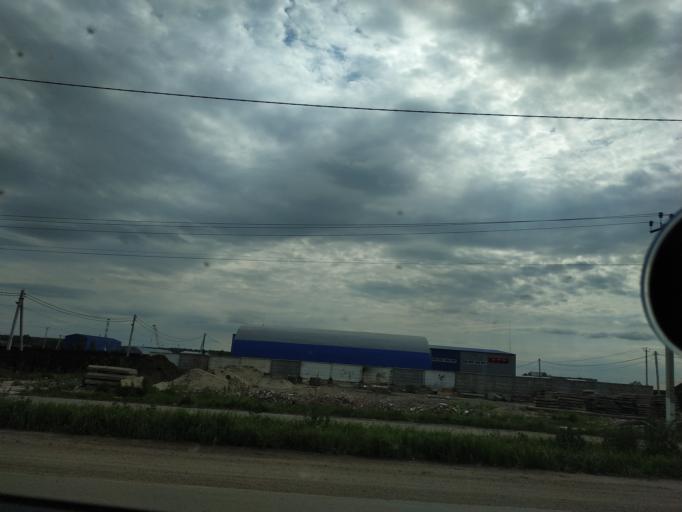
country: RU
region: Moskovskaya
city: Malyshevo
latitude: 55.4939
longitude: 38.3115
